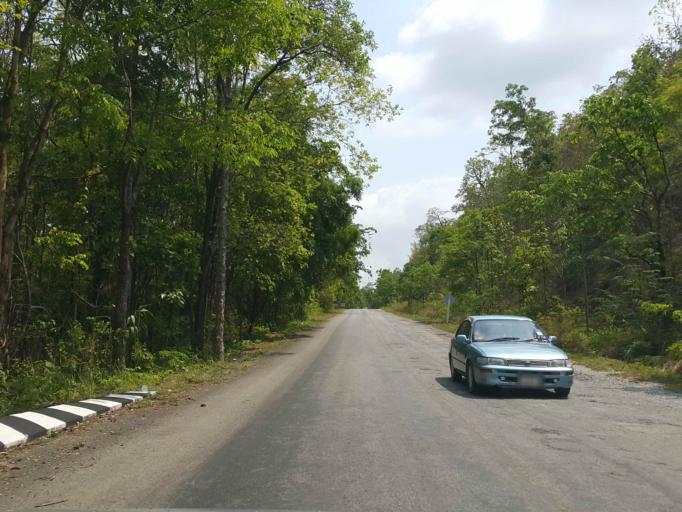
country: TH
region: Lampang
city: Thoen
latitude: 17.6258
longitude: 99.3130
